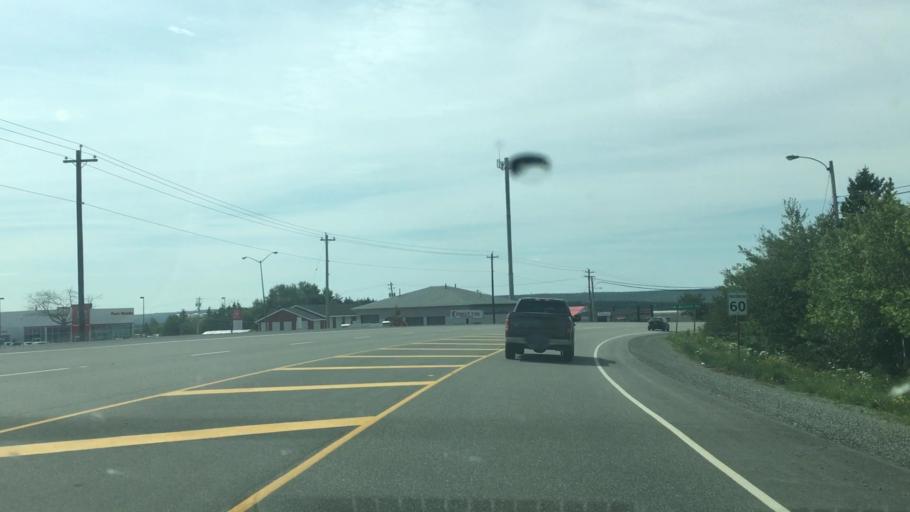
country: CA
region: Nova Scotia
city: Port Hawkesbury
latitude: 45.6172
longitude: -61.3359
